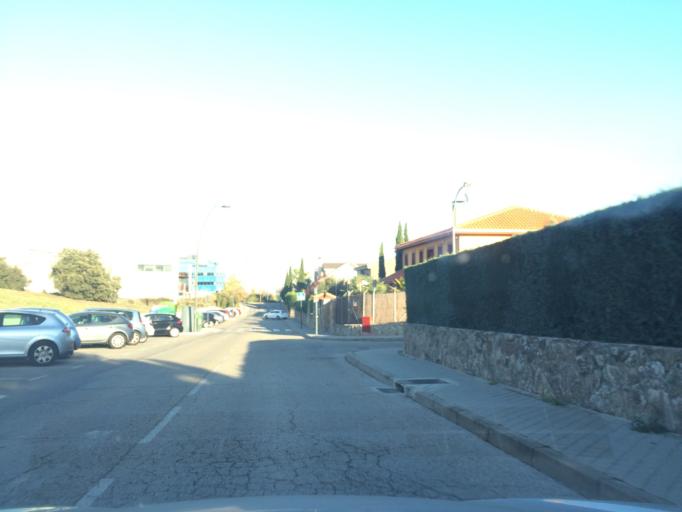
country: ES
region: Madrid
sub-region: Provincia de Madrid
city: Tres Cantos
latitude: 40.5893
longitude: -3.7091
